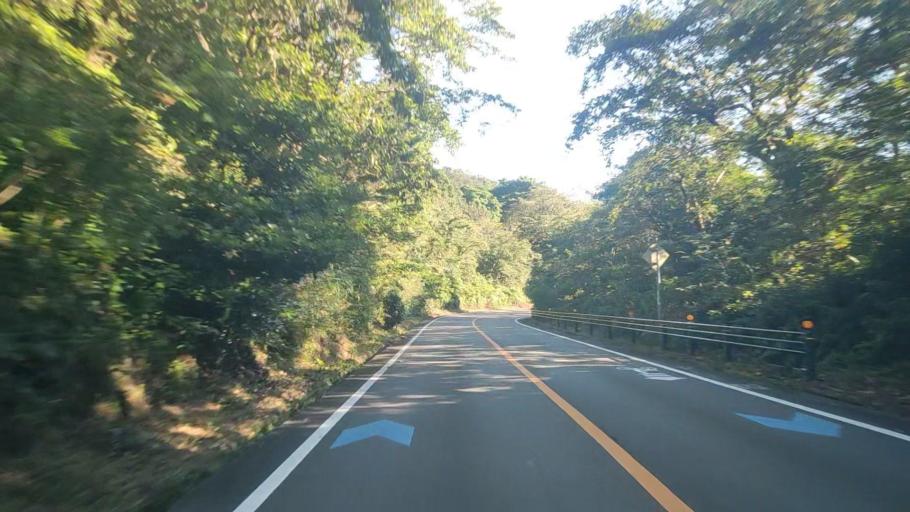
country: JP
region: Mie
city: Toba
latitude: 34.4071
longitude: 136.8905
